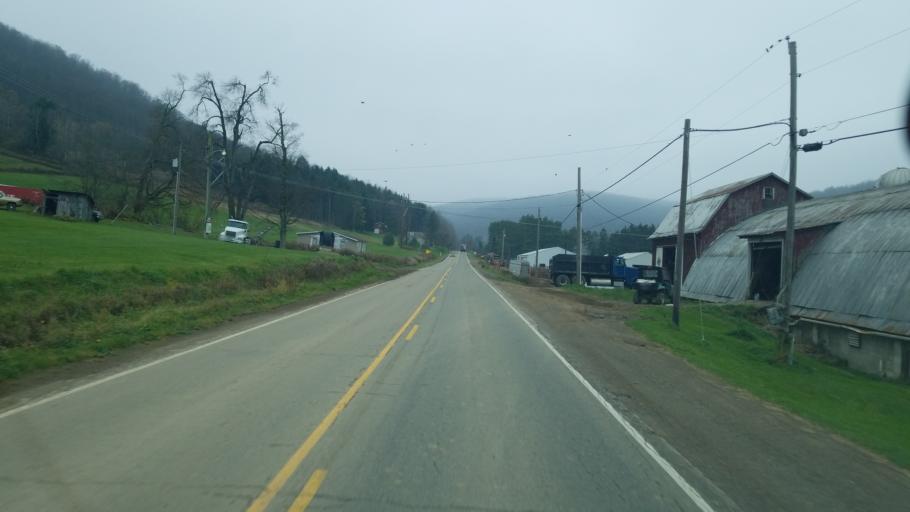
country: US
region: Pennsylvania
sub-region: McKean County
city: Smethport
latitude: 41.8116
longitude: -78.4745
